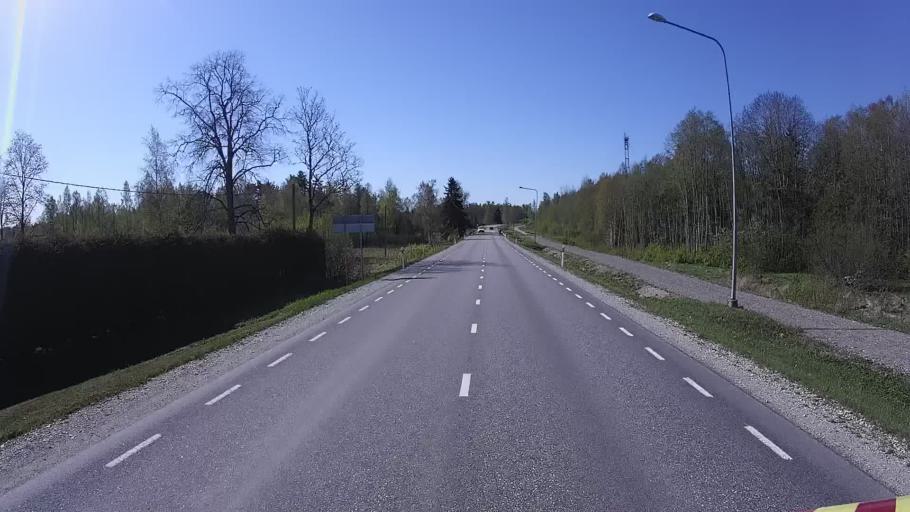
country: EE
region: Raplamaa
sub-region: Jaervakandi vald
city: Jarvakandi
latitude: 58.7877
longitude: 24.8187
